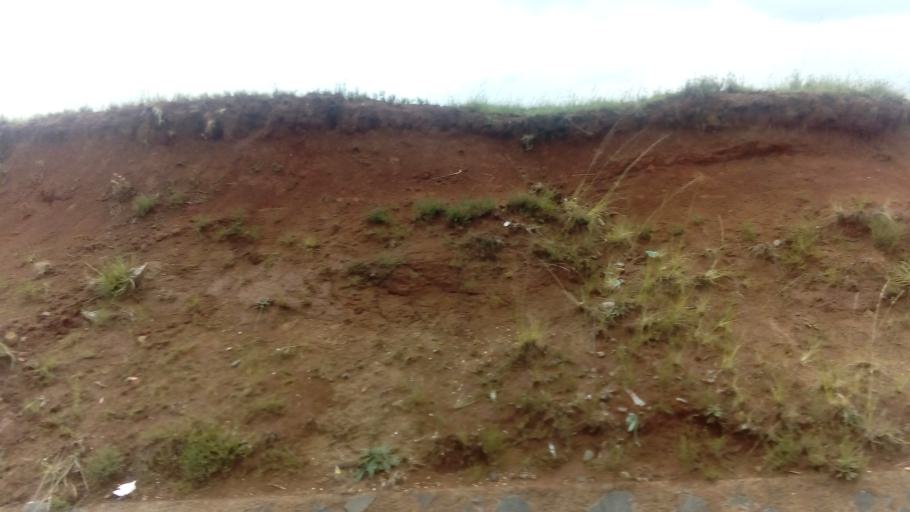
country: LS
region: Butha-Buthe
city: Butha-Buthe
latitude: -29.0327
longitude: 28.2590
